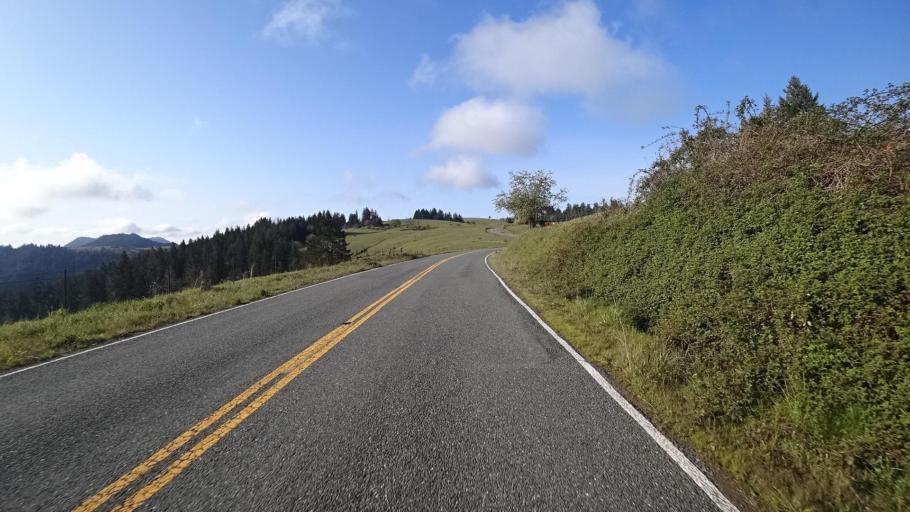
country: US
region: California
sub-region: Humboldt County
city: Blue Lake
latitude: 40.7340
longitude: -123.9468
